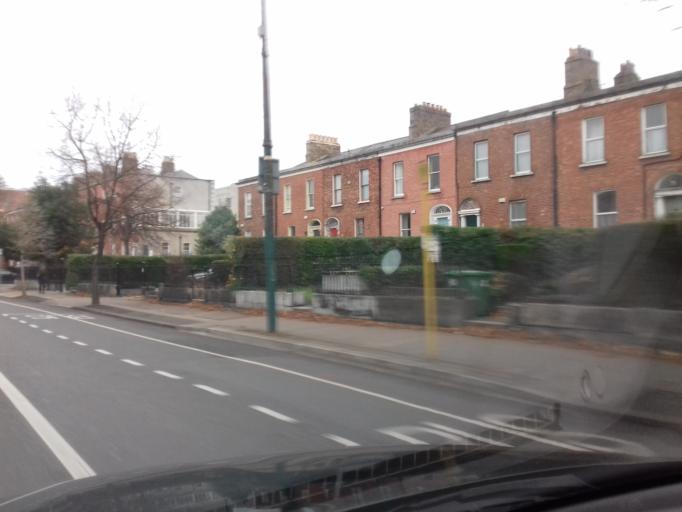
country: IE
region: Leinster
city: Rathmines
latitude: 53.3287
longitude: -6.2587
